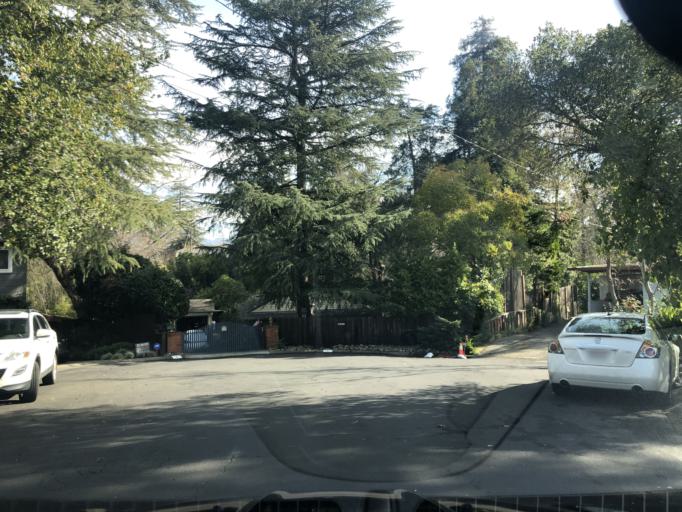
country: US
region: California
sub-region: Contra Costa County
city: Saranap
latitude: 37.8903
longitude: -122.0836
